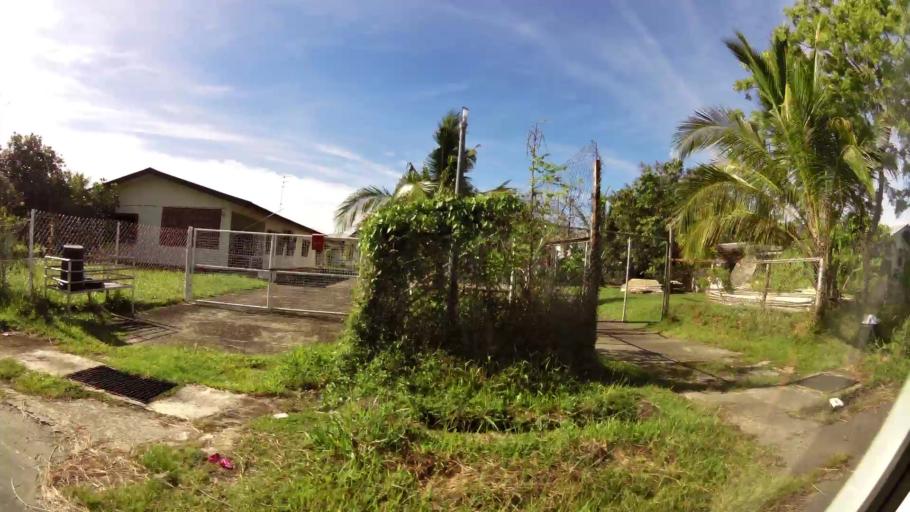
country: BN
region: Belait
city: Kuala Belait
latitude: 4.5861
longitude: 114.2170
